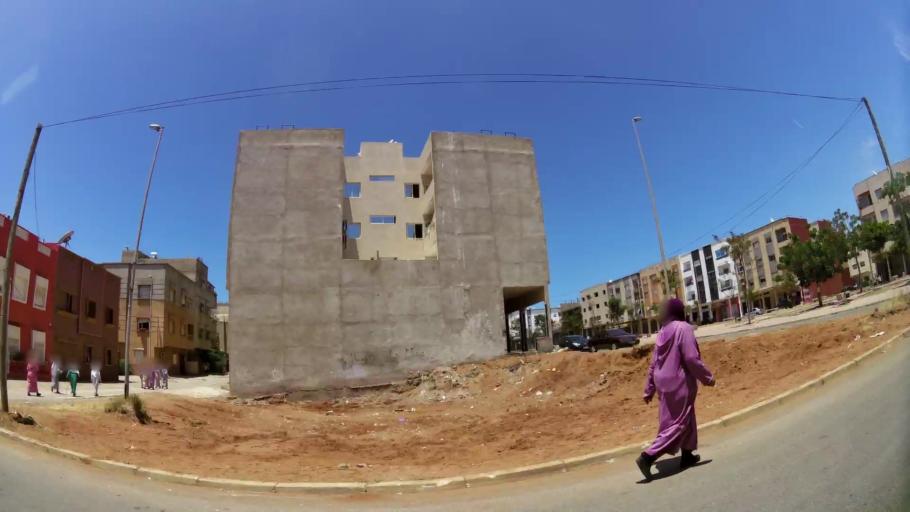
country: MA
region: Gharb-Chrarda-Beni Hssen
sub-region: Kenitra Province
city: Kenitra
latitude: 34.2510
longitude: -6.6194
